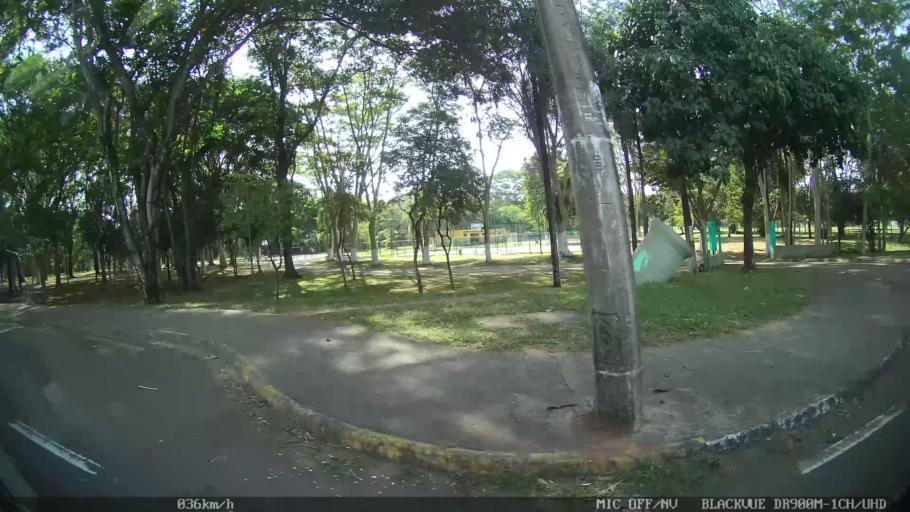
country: BR
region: Sao Paulo
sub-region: Piracicaba
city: Piracicaba
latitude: -22.7266
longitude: -47.6683
